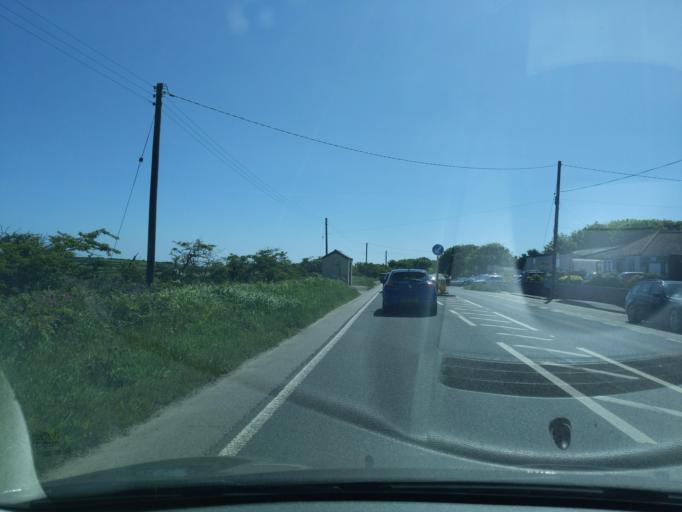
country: GB
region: England
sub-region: Cornwall
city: Wendron
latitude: 50.1544
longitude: -5.1921
